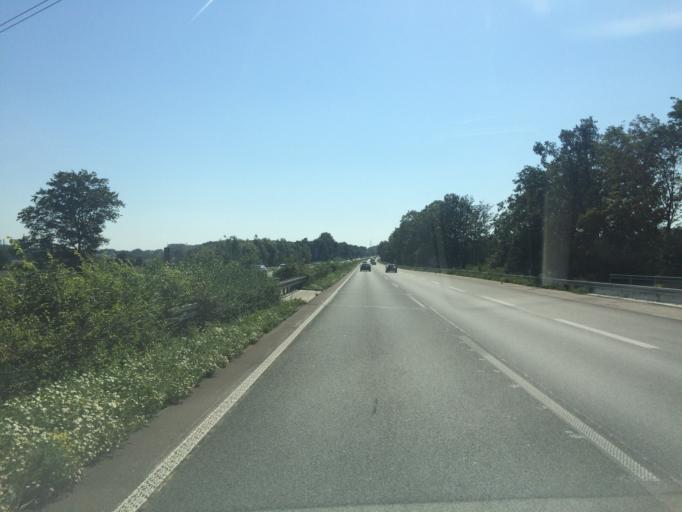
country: DE
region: North Rhine-Westphalia
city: Werne
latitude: 51.6927
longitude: 7.6696
